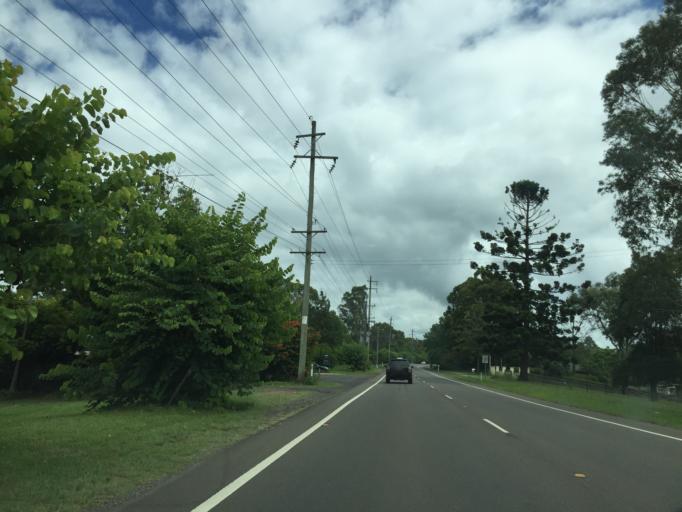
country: AU
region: New South Wales
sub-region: Hawkesbury
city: Richmond
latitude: -33.5558
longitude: 150.6984
